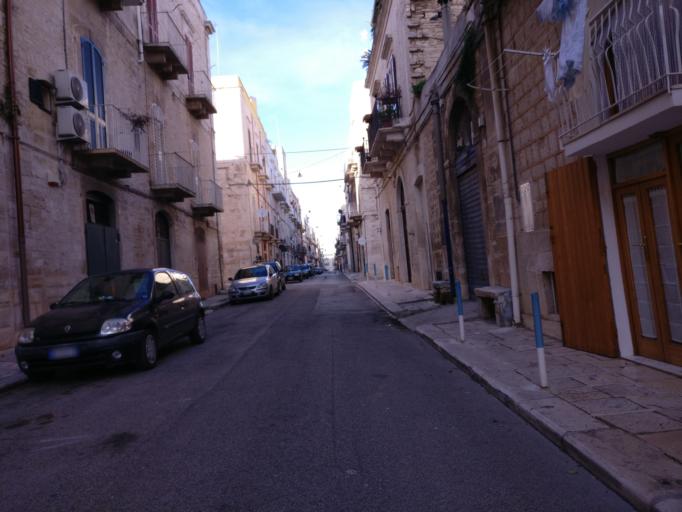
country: IT
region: Apulia
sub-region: Provincia di Bari
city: Ruvo di Puglia
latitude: 41.1157
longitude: 16.4879
